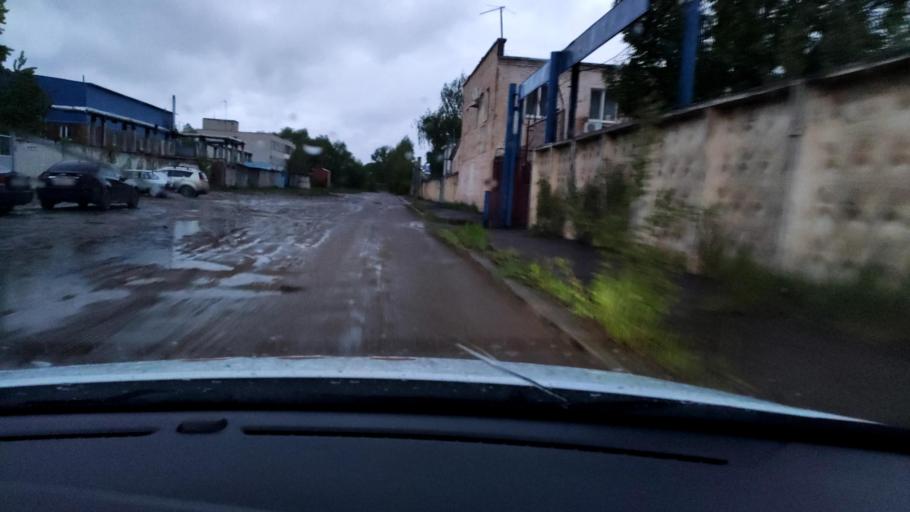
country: RU
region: Tatarstan
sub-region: Gorod Kazan'
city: Kazan
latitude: 55.7195
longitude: 49.1245
